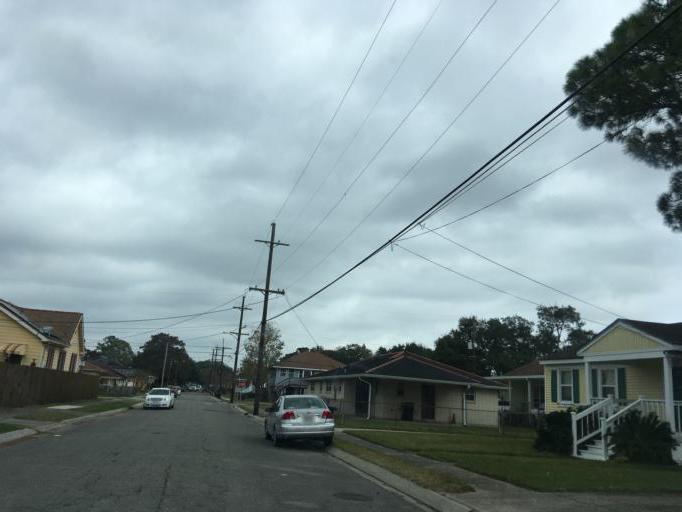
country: US
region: Louisiana
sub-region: Orleans Parish
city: New Orleans
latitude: 29.9934
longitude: -90.0575
